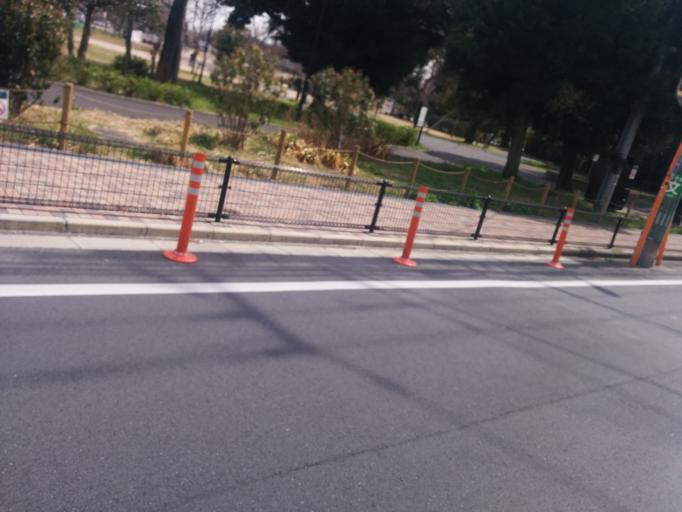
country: JP
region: Tokyo
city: Tokyo
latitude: 35.6868
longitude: 139.6469
